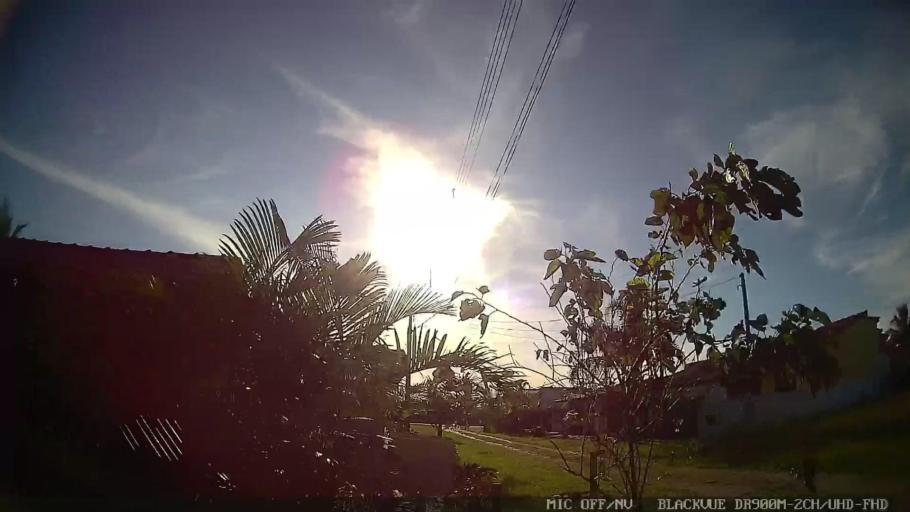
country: BR
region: Sao Paulo
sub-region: Iguape
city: Iguape
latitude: -24.7594
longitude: -47.5712
